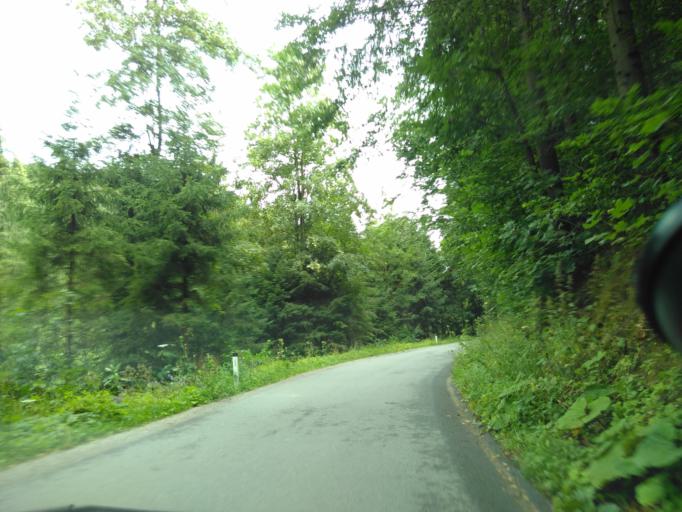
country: AT
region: Styria
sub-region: Politischer Bezirk Graz-Umgebung
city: Semriach
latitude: 47.2271
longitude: 15.3999
